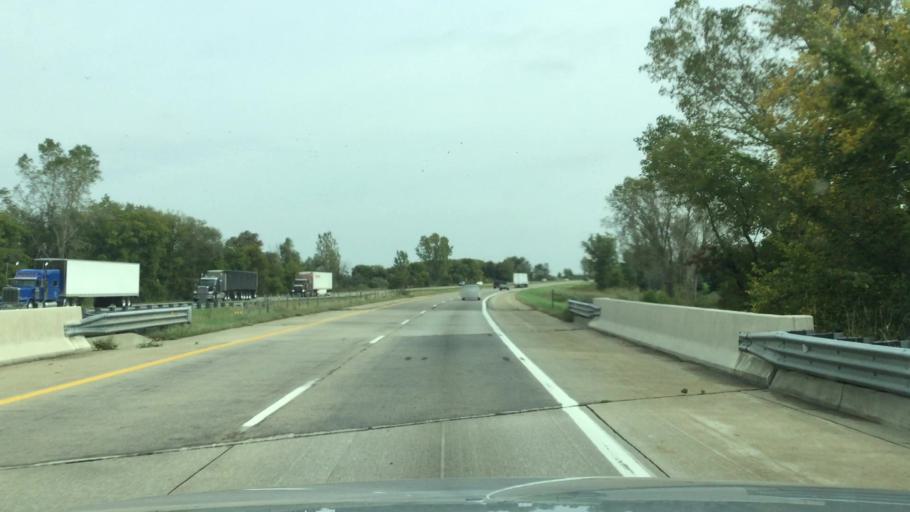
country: US
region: Michigan
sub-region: Shiawassee County
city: Durand
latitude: 42.9561
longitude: -83.9691
